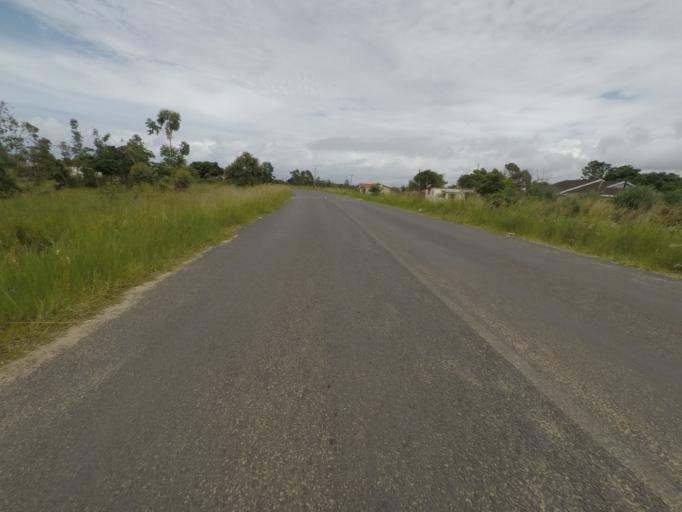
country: ZA
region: KwaZulu-Natal
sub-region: uThungulu District Municipality
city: eSikhawini
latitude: -28.9070
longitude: 31.8823
